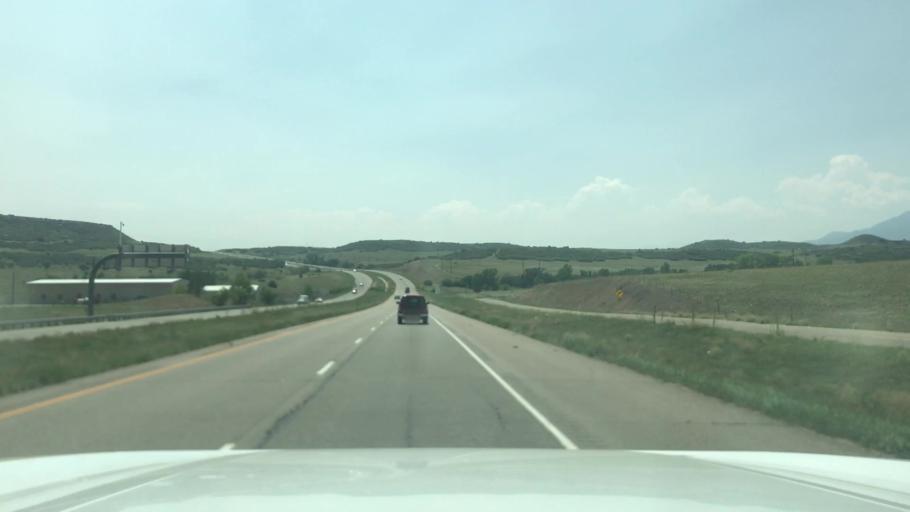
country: US
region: Colorado
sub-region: Pueblo County
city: Colorado City
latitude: 37.9177
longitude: -104.8259
